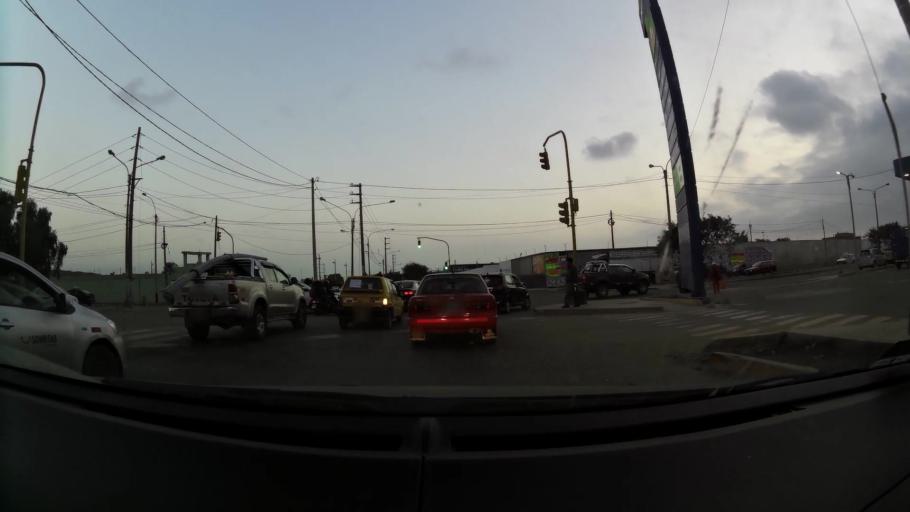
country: PE
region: La Libertad
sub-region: Provincia de Trujillo
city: El Porvenir
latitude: -8.0924
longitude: -79.0181
